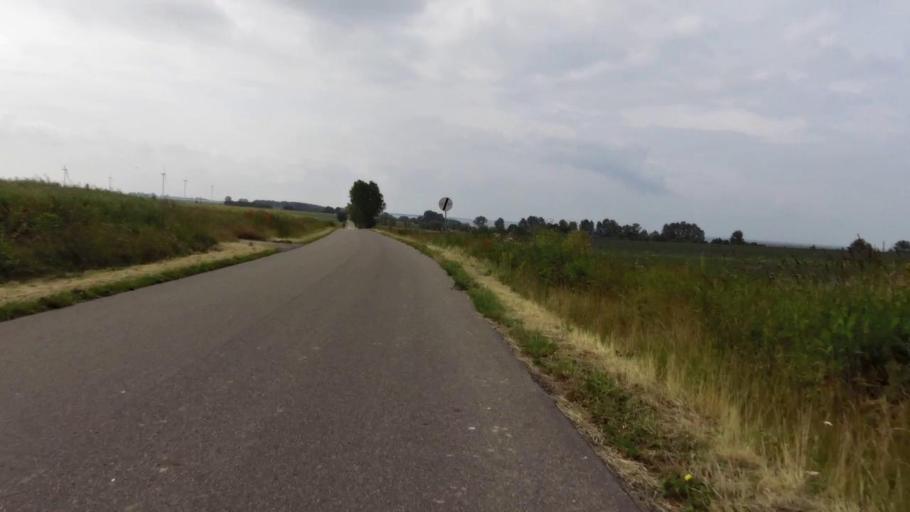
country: PL
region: West Pomeranian Voivodeship
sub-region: Powiat kamienski
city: Wolin
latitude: 53.8200
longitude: 14.6150
